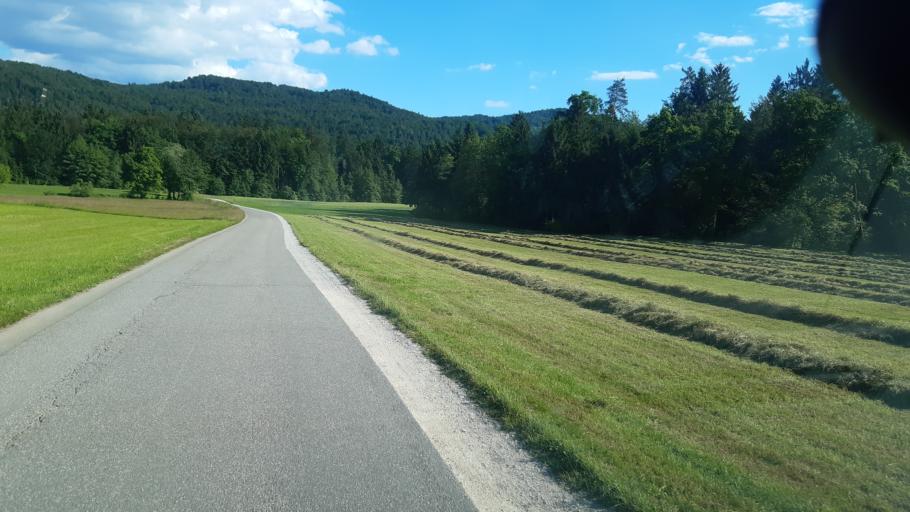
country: SI
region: Vodice
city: Vodice
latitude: 46.1681
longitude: 14.5148
